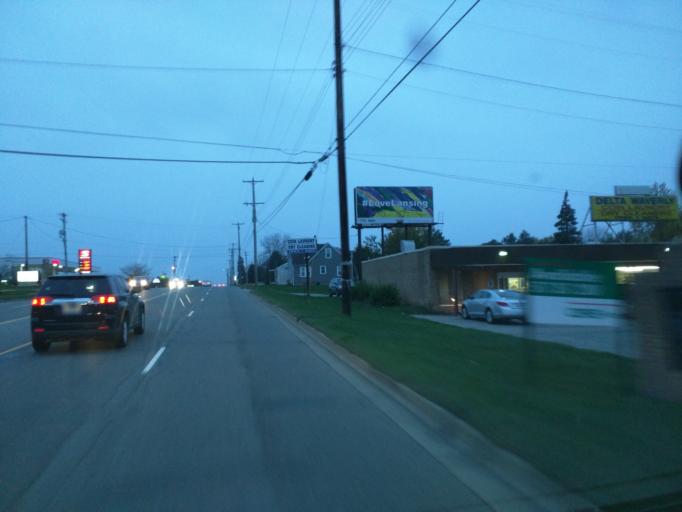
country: US
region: Michigan
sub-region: Ingham County
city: Edgemont Park
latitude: 42.7308
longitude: -84.6031
